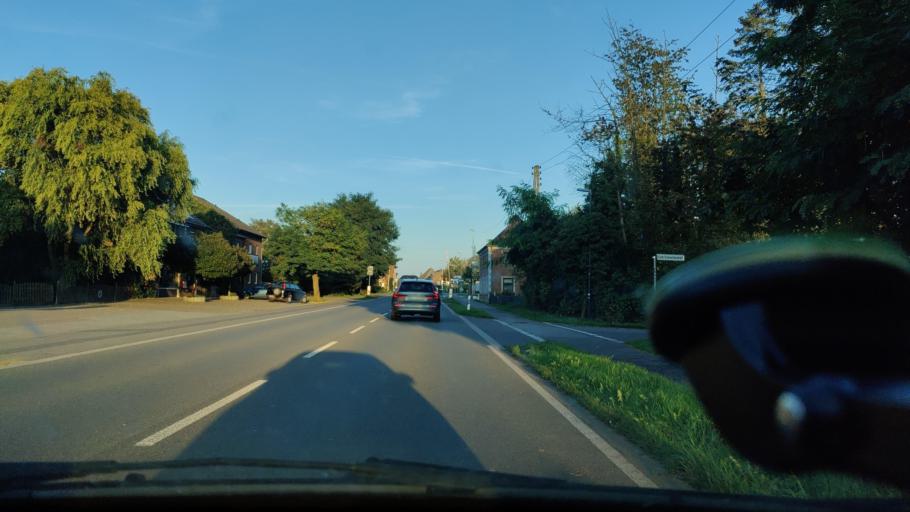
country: DE
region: North Rhine-Westphalia
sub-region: Regierungsbezirk Dusseldorf
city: Mehrhoog
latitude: 51.7392
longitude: 6.5151
